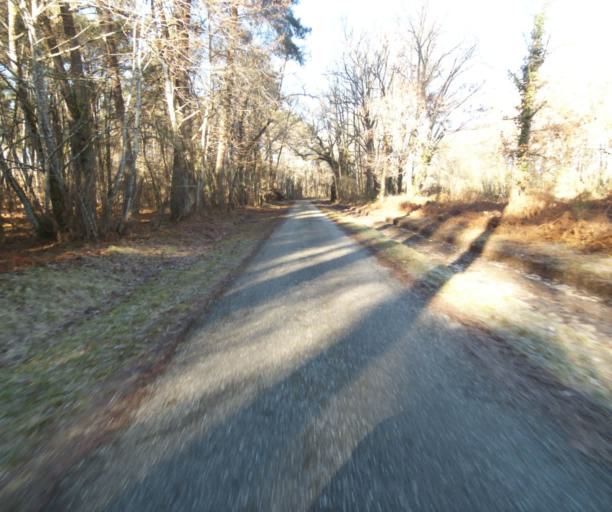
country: FR
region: Aquitaine
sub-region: Departement des Landes
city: Gabarret
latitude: 44.1009
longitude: 0.0815
